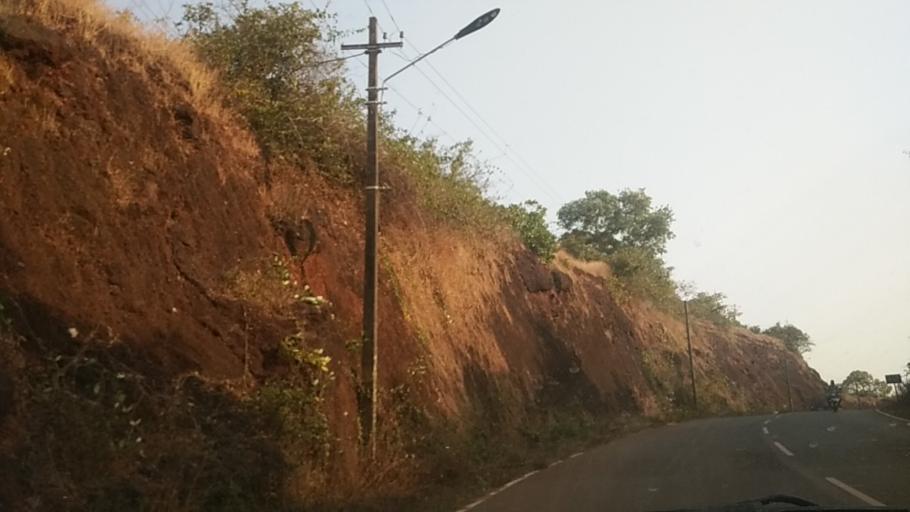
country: IN
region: Goa
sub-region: North Goa
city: Morjim
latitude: 15.6508
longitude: 73.7593
